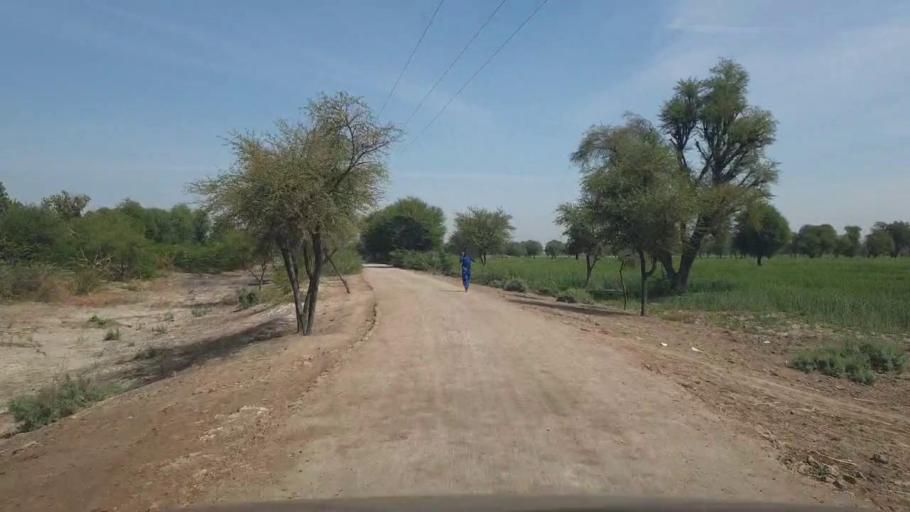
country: PK
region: Sindh
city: Umarkot
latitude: 25.3340
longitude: 69.6200
